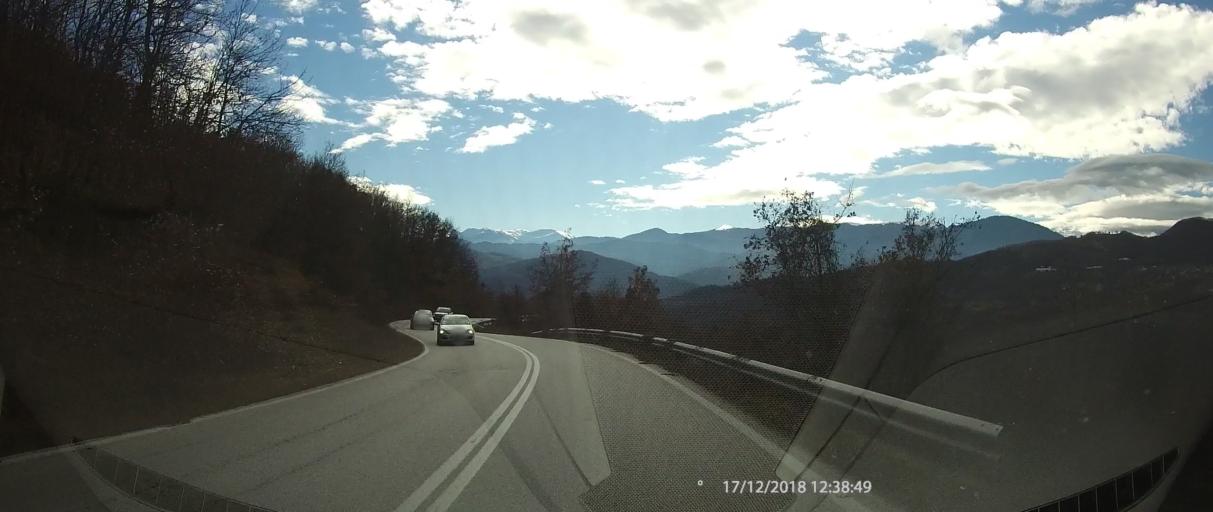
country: GR
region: Epirus
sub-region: Nomos Ioanninon
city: Metsovo
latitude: 39.8050
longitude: 21.3494
